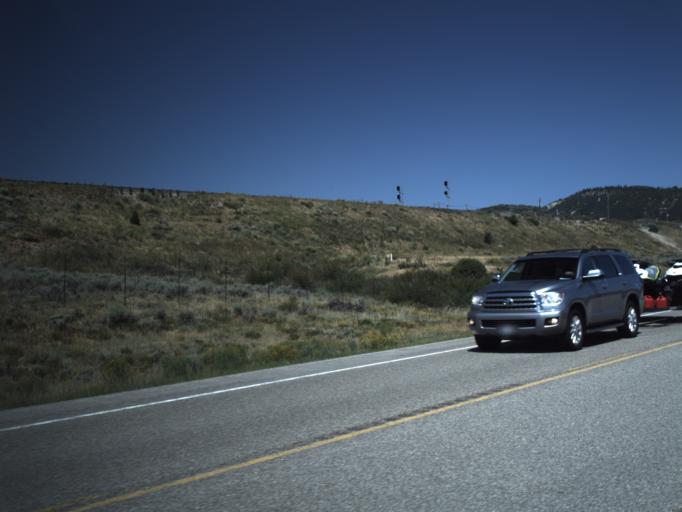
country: US
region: Utah
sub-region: Carbon County
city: Helper
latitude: 39.9115
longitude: -111.0617
